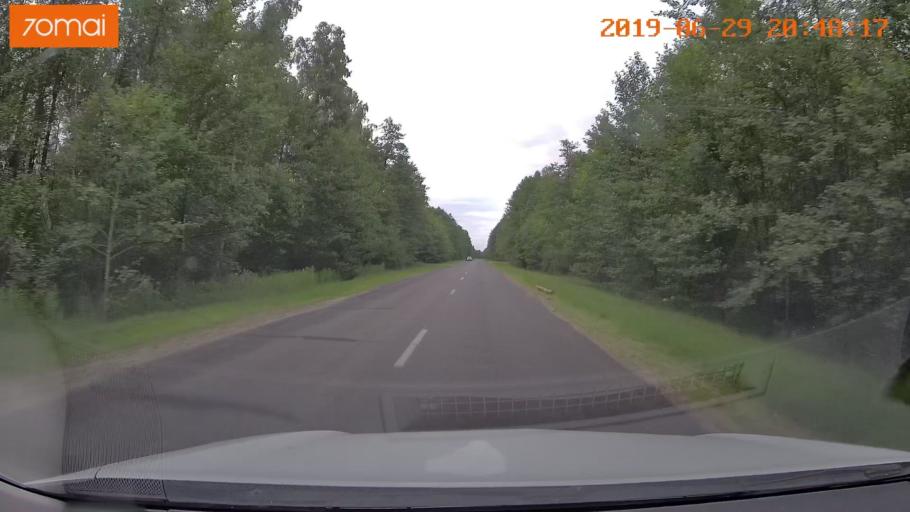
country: BY
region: Brest
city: Hantsavichy
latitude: 52.6487
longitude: 26.3173
